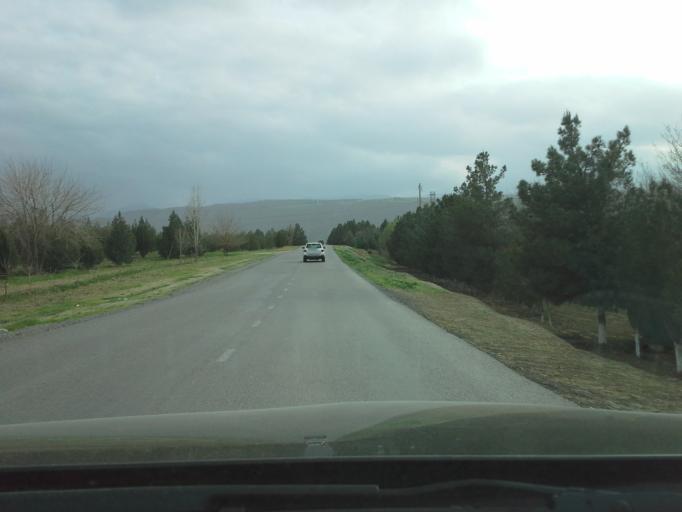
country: TM
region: Ahal
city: Abadan
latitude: 37.9516
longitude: 58.2276
